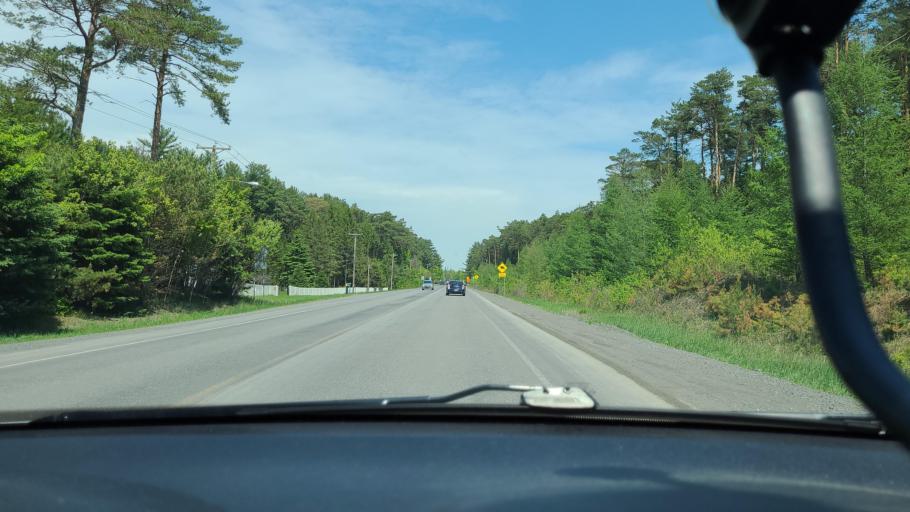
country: CA
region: Quebec
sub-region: Laurentides
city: Lachute
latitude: 45.6642
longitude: -74.2470
